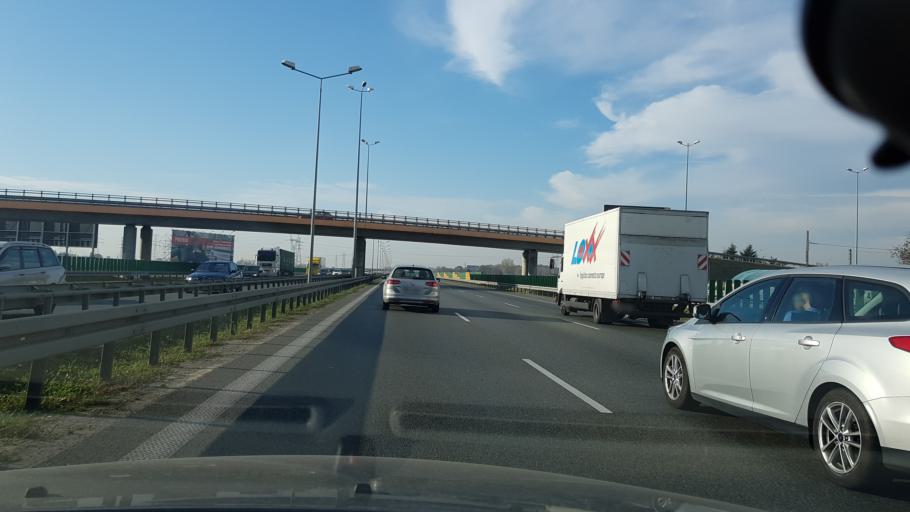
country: PL
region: Masovian Voivodeship
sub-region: Powiat warszawski zachodni
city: Babice
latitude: 52.2288
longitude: 20.8771
